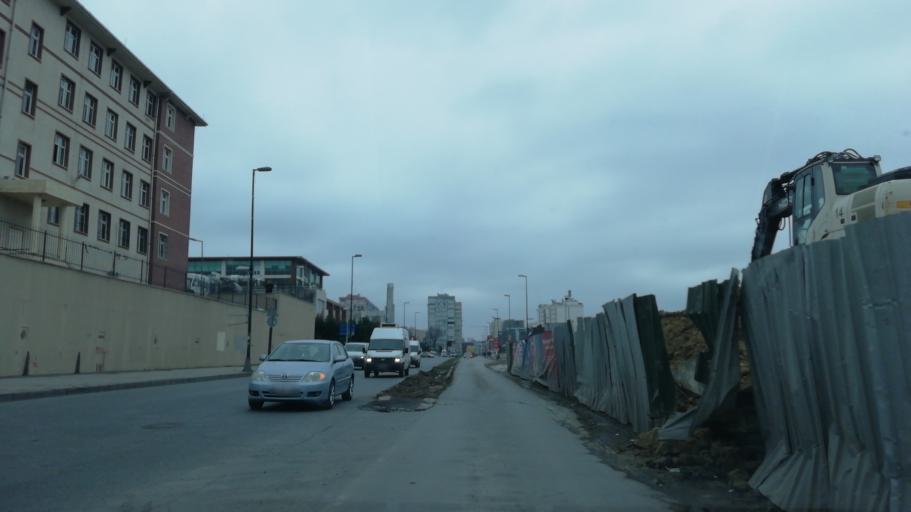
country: TR
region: Istanbul
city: Mahmutbey
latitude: 41.0150
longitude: 28.8181
